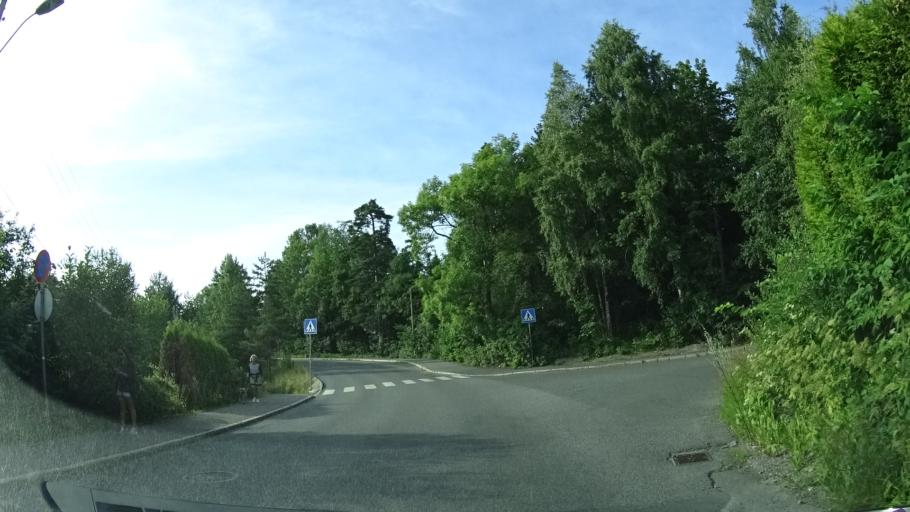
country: NO
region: Oslo
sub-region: Oslo
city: Sjolyststranda
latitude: 59.9622
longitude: 10.6471
